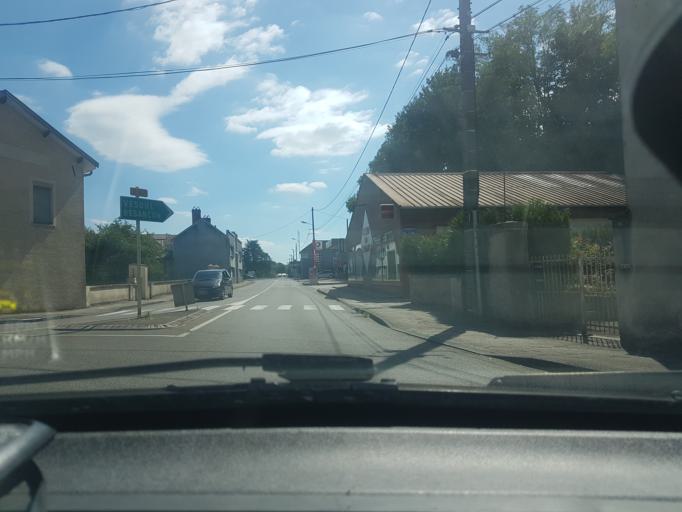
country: FR
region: Franche-Comte
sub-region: Departement de la Haute-Saone
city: Gray
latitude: 47.4453
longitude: 5.5978
